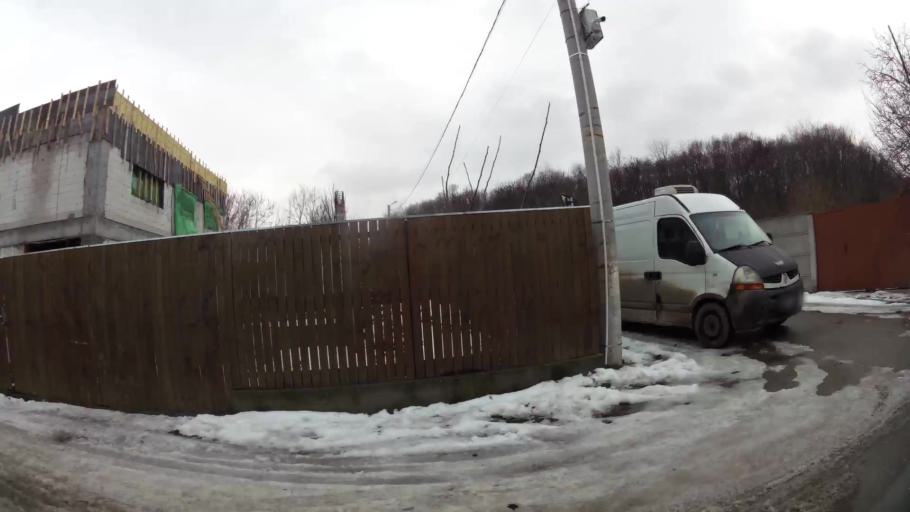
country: RO
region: Ilfov
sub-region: Comuna Tunari
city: Tunari
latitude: 44.5448
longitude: 26.1296
